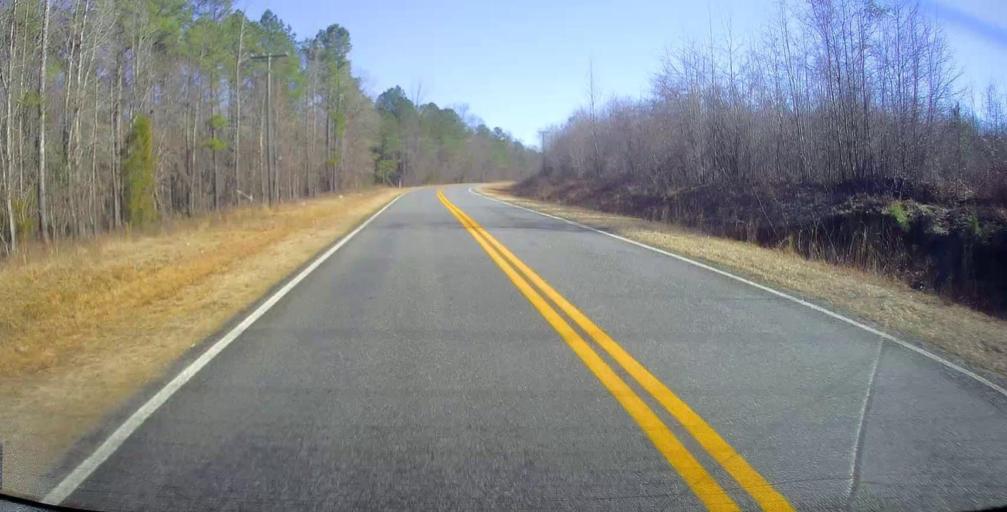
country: US
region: Georgia
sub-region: Crawford County
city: Knoxville
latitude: 32.7062
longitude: -83.9949
